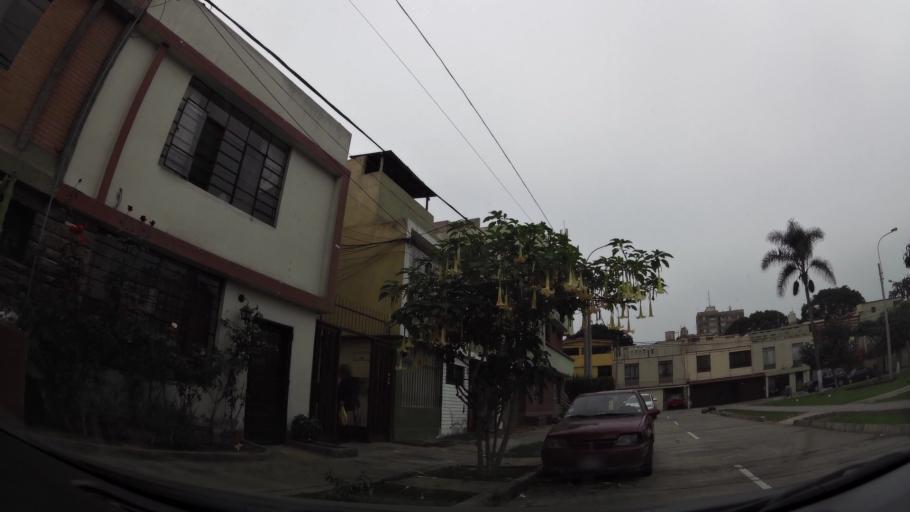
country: PE
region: Lima
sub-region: Lima
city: San Isidro
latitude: -12.0797
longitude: -77.0652
